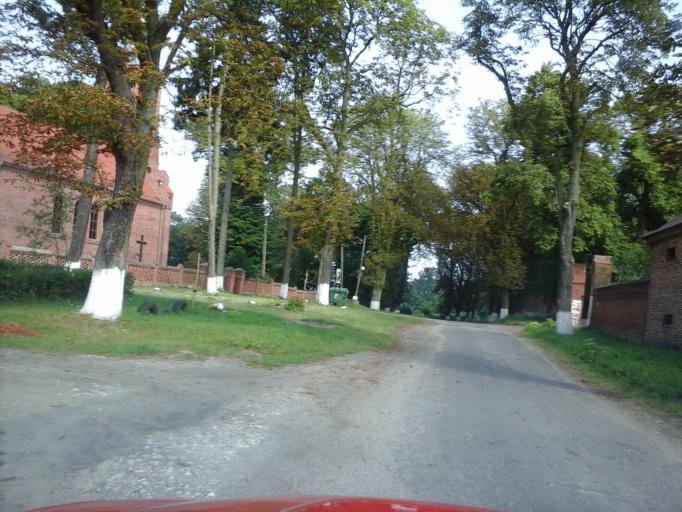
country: PL
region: West Pomeranian Voivodeship
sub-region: Powiat choszczenski
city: Pelczyce
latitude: 53.0643
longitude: 15.2430
